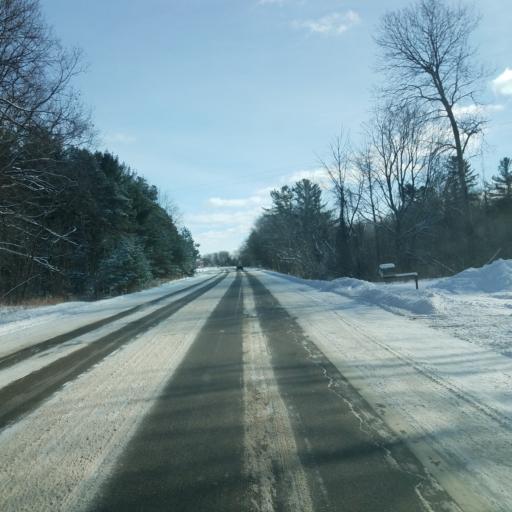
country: US
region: Michigan
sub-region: Isabella County
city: Lake Isabella
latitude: 43.8579
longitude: -85.0092
